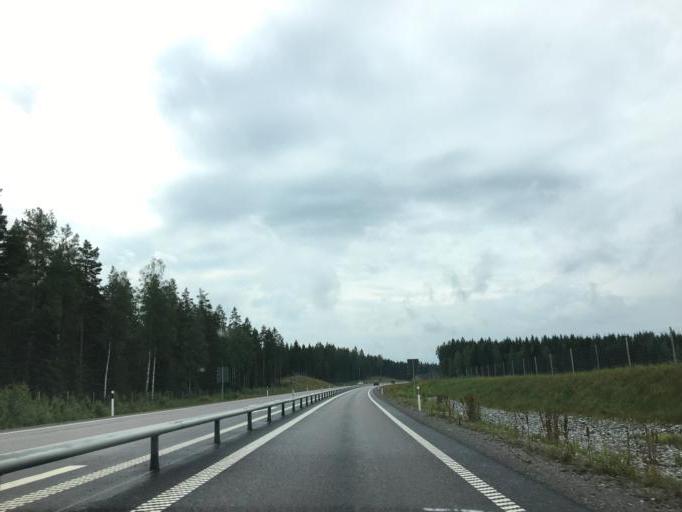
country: SE
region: Soedermanland
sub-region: Katrineholms Kommun
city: Katrineholm
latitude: 58.9827
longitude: 16.2655
